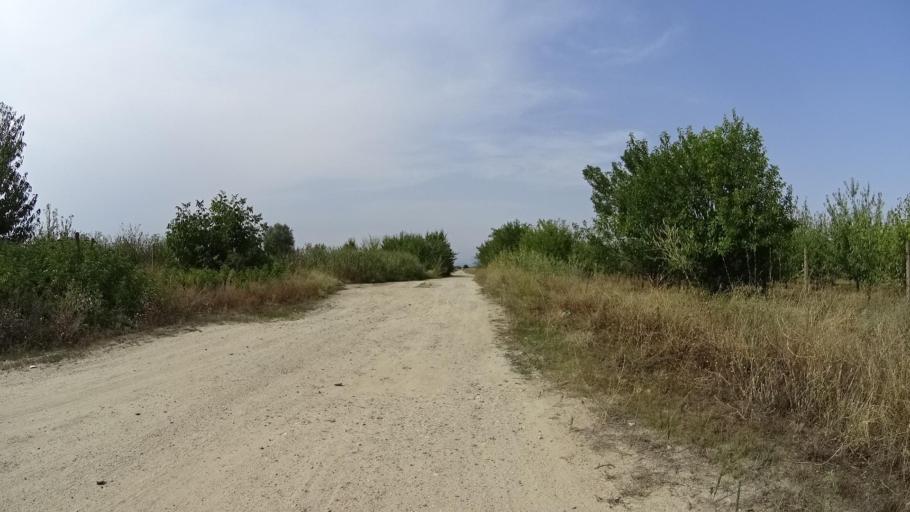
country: BG
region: Plovdiv
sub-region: Obshtina Kaloyanovo
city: Kaloyanovo
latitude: 42.2778
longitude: 24.7998
